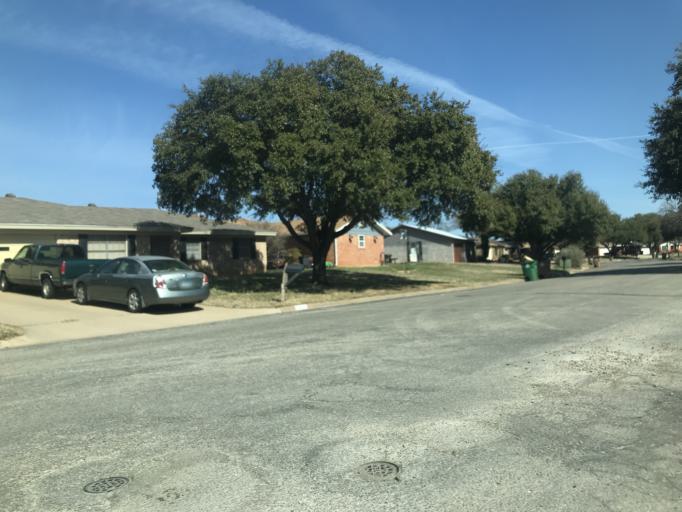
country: US
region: Texas
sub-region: Tom Green County
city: San Angelo
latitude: 31.4336
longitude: -100.4845
